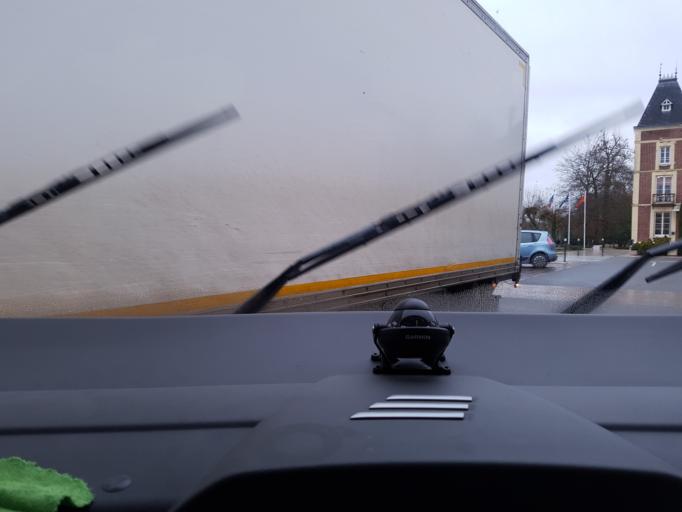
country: FR
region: Haute-Normandie
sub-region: Departement de l'Eure
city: Beaumont-le-Roger
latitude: 49.0804
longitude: 0.7775
